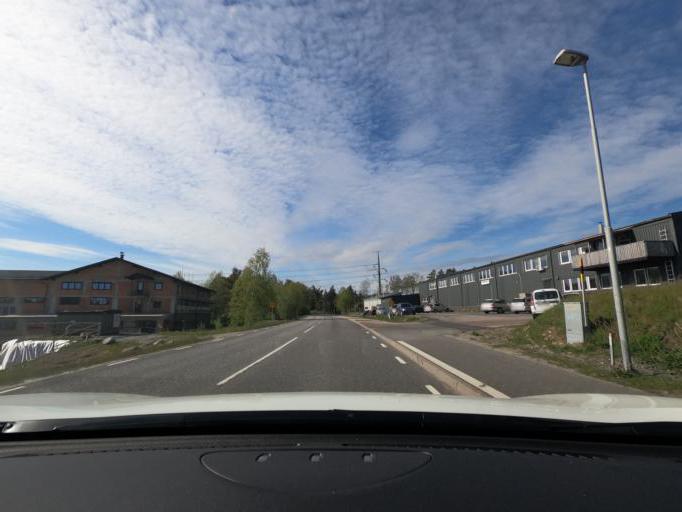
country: SE
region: Vaestra Goetaland
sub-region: Harryda Kommun
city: Landvetter
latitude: 57.6776
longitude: 12.2415
